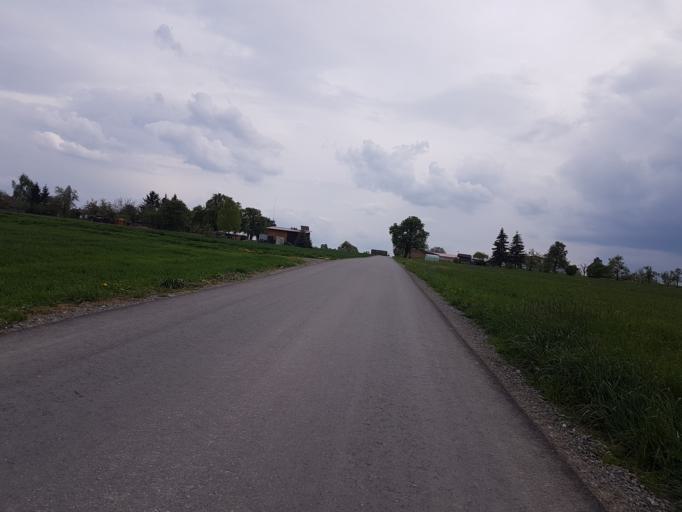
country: DE
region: Baden-Wuerttemberg
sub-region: Regierungsbezirk Stuttgart
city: Bondorf
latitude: 48.5256
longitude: 8.8221
